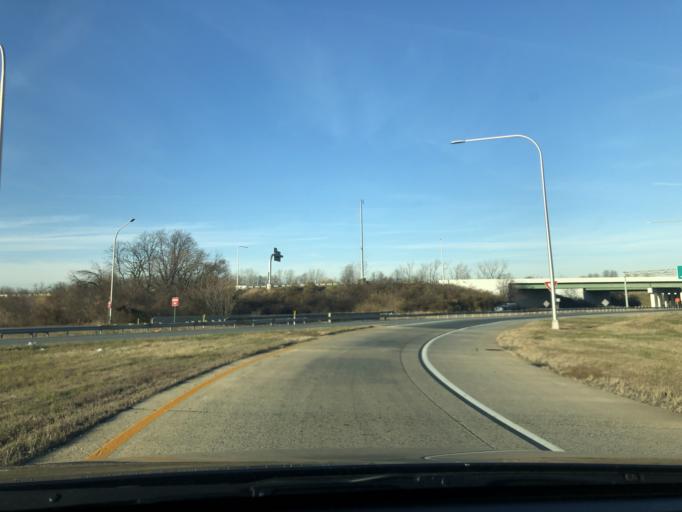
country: US
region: Delaware
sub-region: New Castle County
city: Wilmington
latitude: 39.7154
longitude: -75.5582
